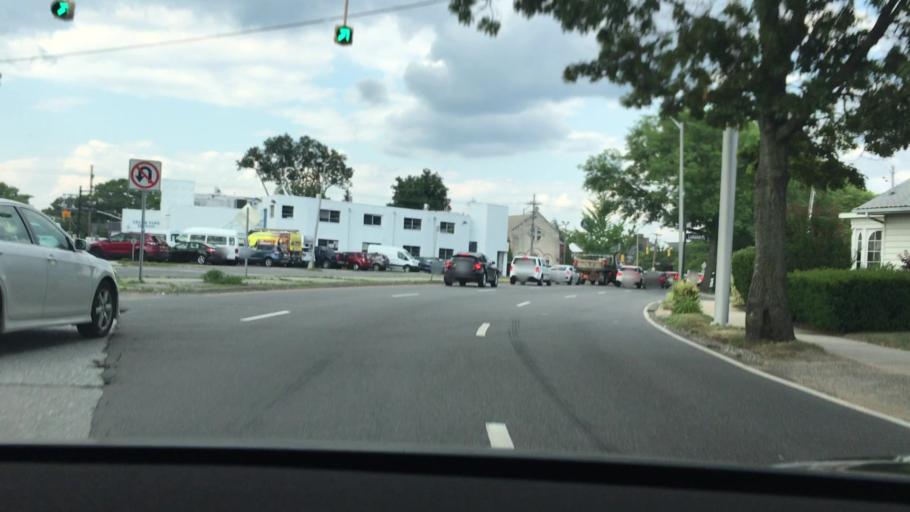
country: US
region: New York
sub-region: Nassau County
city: Lynbrook
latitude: 40.6573
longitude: -73.6769
